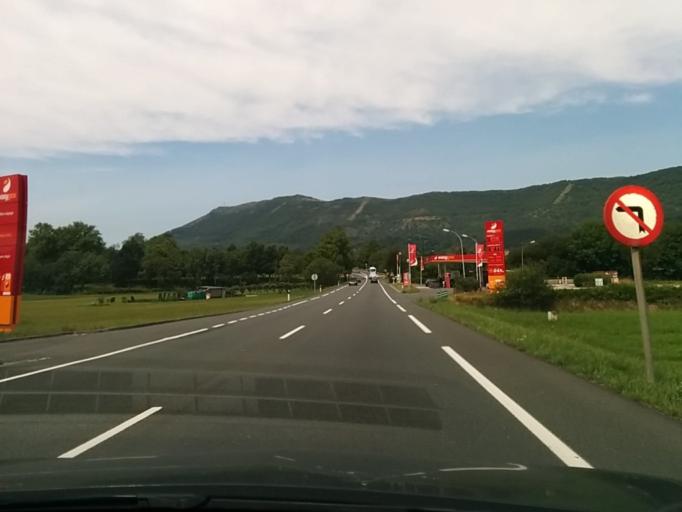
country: ES
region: Basque Country
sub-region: Provincia de Guipuzcoa
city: Irun
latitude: 43.3471
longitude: -1.8074
